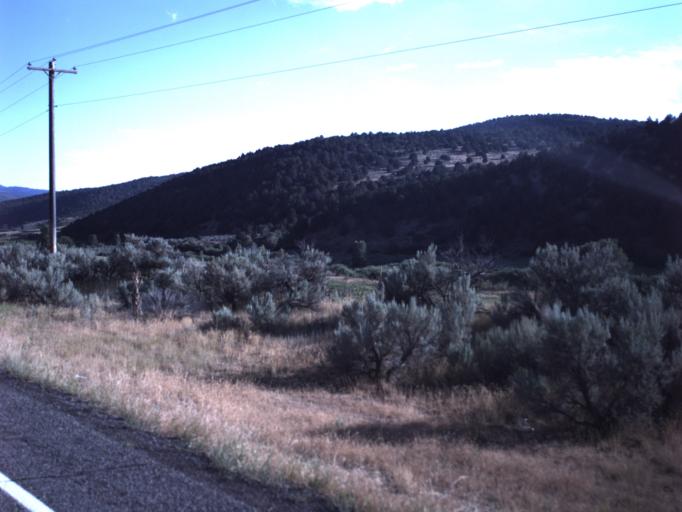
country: US
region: Utah
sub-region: Utah County
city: Woodland Hills
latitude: 39.9127
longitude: -111.5506
